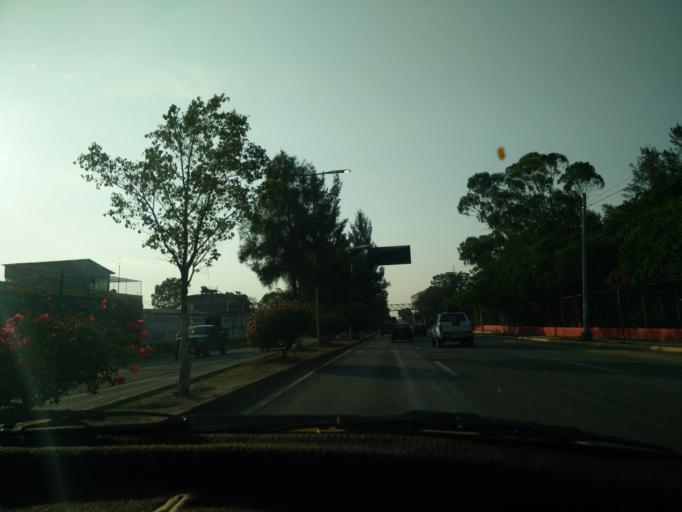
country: MX
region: Oaxaca
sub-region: Santa Maria Atzompa
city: San Jeronimo Yahuiche
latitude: 17.1170
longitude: -96.7597
